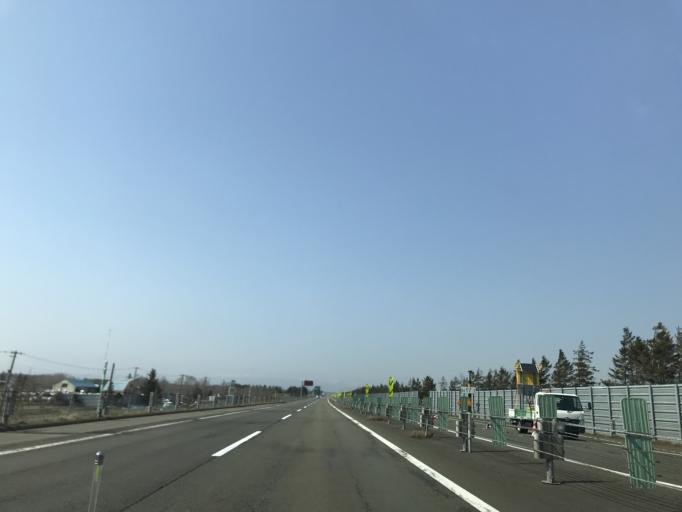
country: JP
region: Hokkaido
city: Ebetsu
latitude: 43.1096
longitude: 141.6093
